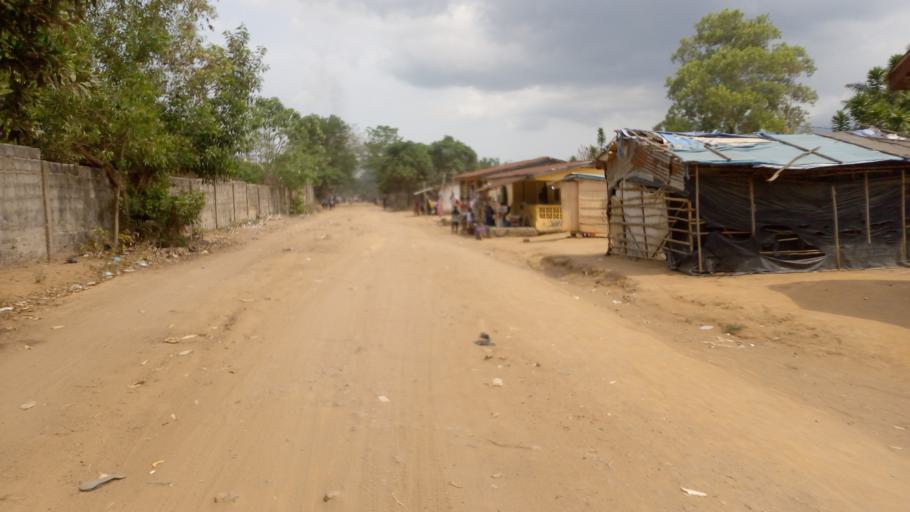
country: SL
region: Western Area
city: Waterloo
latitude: 8.3182
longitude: -13.0650
